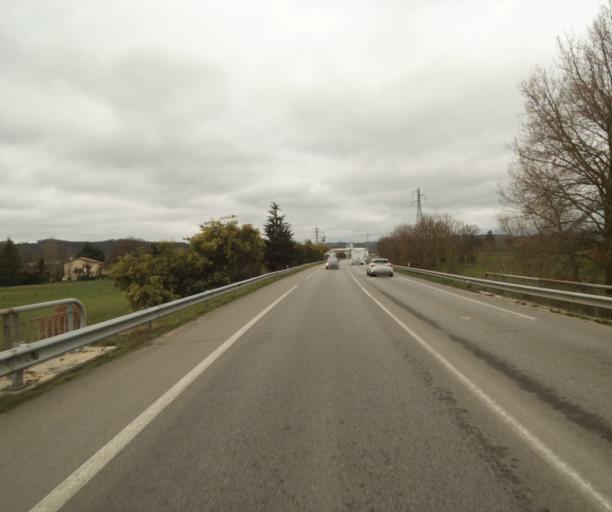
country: FR
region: Midi-Pyrenees
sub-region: Departement de l'Ariege
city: Pamiers
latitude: 43.1384
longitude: 1.6113
